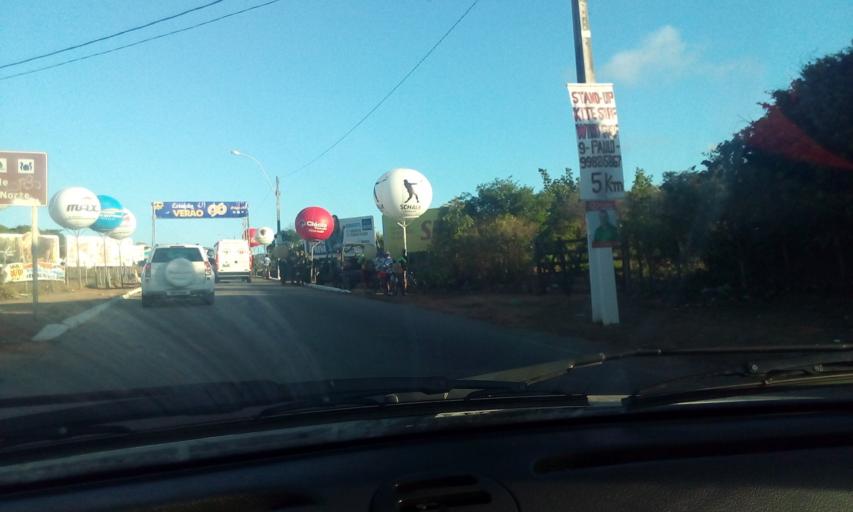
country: BR
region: Rio Grande do Norte
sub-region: Parnamirim
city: Parnamirim
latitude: -5.9689
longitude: -35.1382
